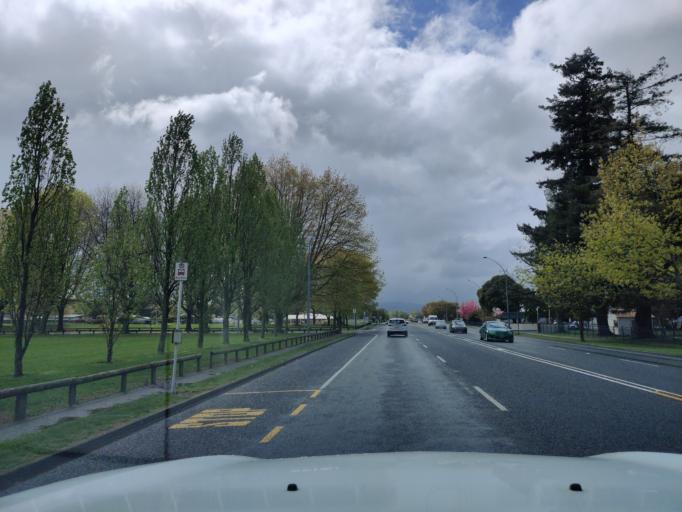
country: NZ
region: Bay of Plenty
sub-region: Rotorua District
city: Rotorua
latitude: -38.1368
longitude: 176.2369
